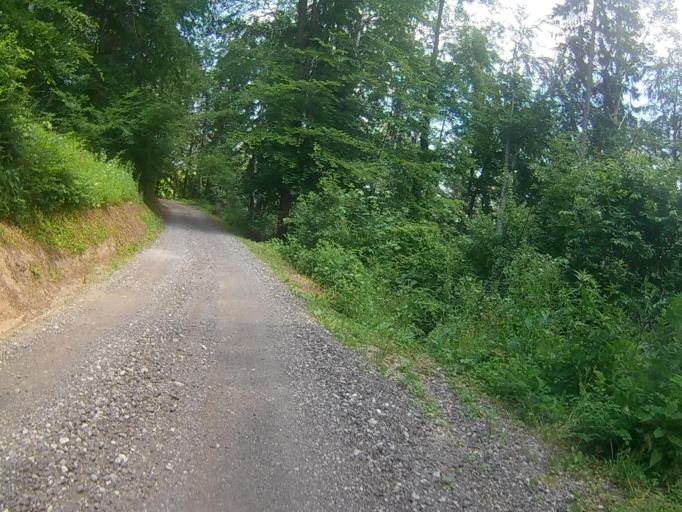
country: SI
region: Kungota
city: Zgornja Kungota
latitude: 46.6220
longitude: 15.6126
